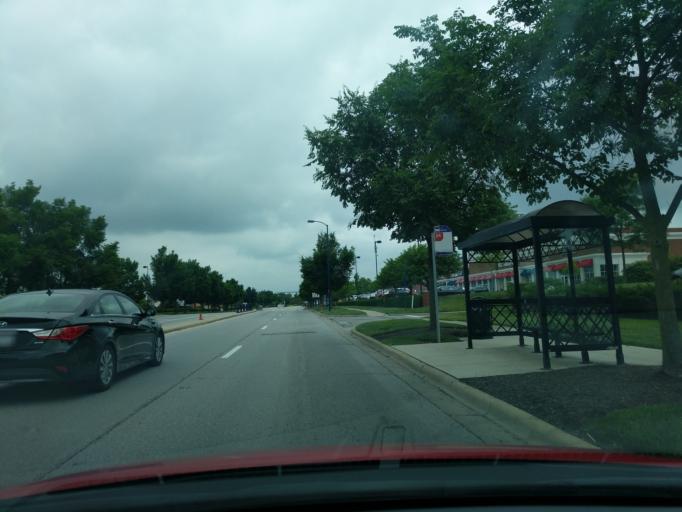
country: US
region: Ohio
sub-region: Franklin County
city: Minerva Park
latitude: 40.0493
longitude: -82.9201
